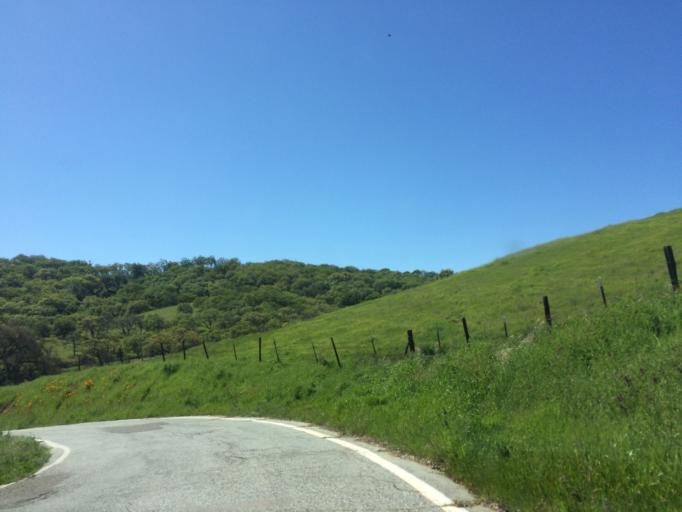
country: US
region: California
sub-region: Santa Clara County
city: Morgan Hill
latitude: 37.1721
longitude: -121.5687
